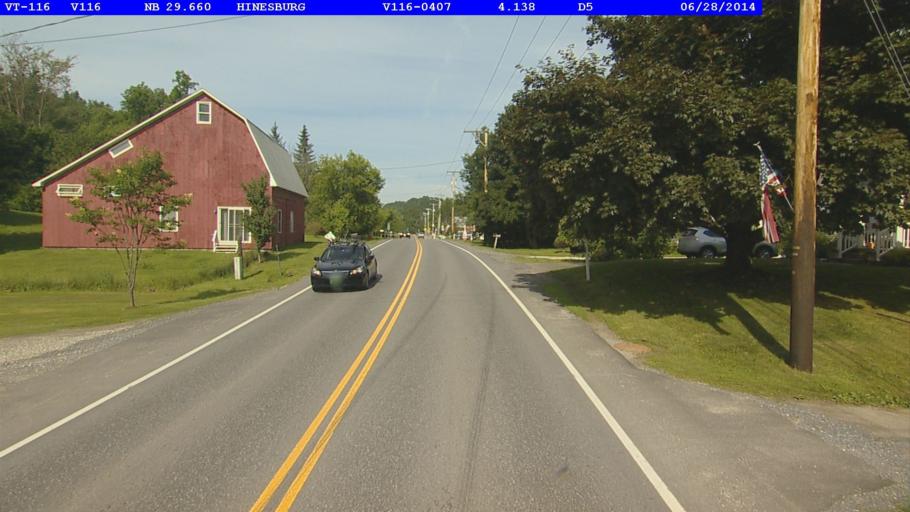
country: US
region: Vermont
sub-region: Chittenden County
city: Hinesburg
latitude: 44.3270
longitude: -73.1050
